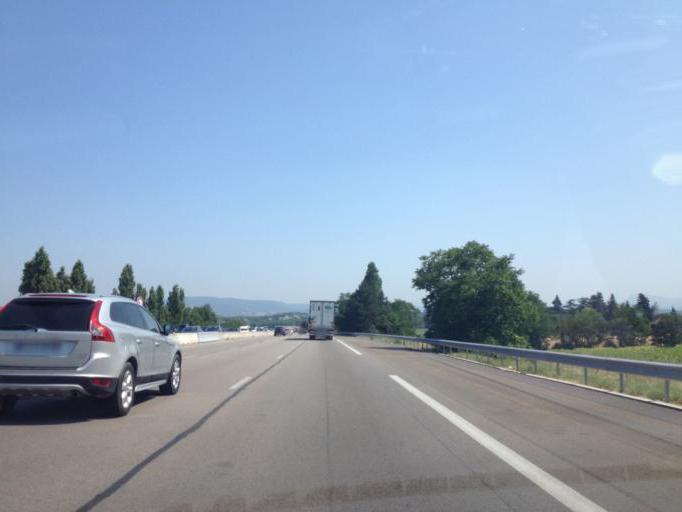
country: FR
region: Rhone-Alpes
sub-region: Departement de la Drome
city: Montboucher-sur-Jabron
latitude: 44.5303
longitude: 4.8005
